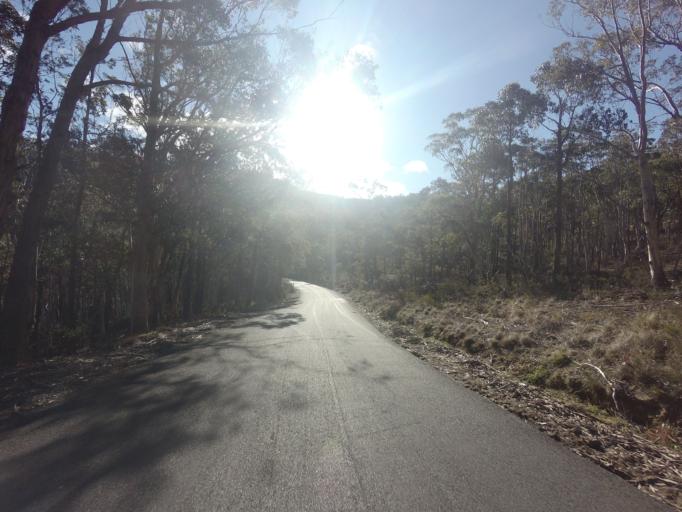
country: AU
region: Tasmania
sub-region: Glenorchy
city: Berriedale
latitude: -42.8213
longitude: 147.1925
